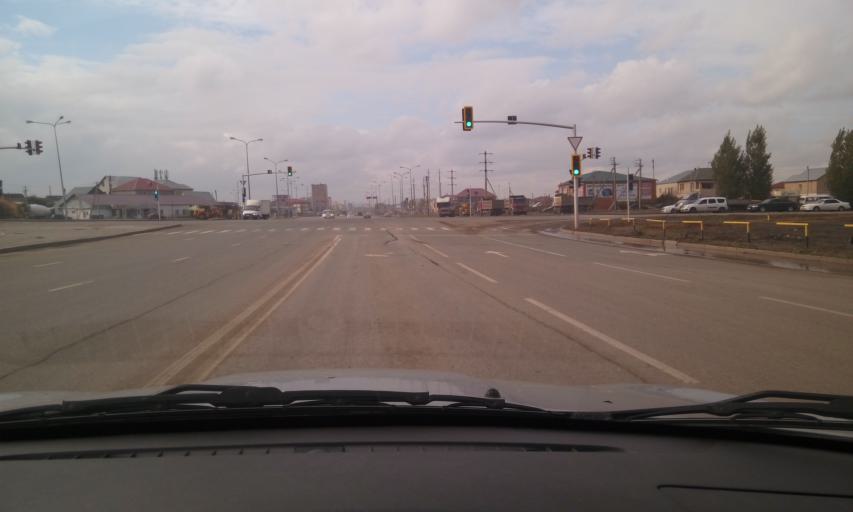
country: KZ
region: Astana Qalasy
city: Astana
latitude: 51.1369
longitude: 71.5225
